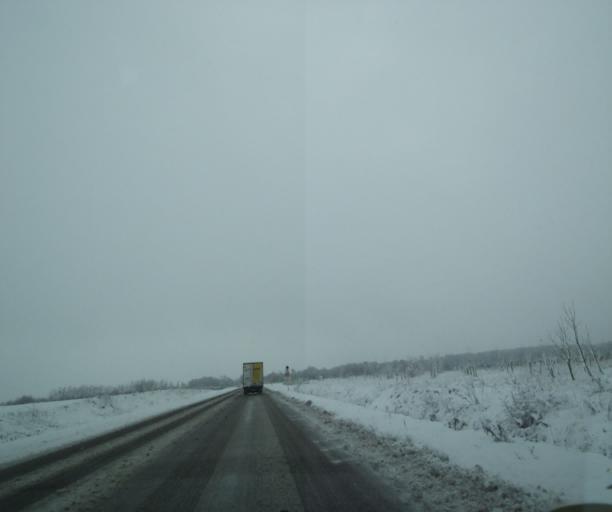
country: FR
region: Champagne-Ardenne
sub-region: Departement de la Haute-Marne
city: Saint-Dizier
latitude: 48.5923
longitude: 4.8912
